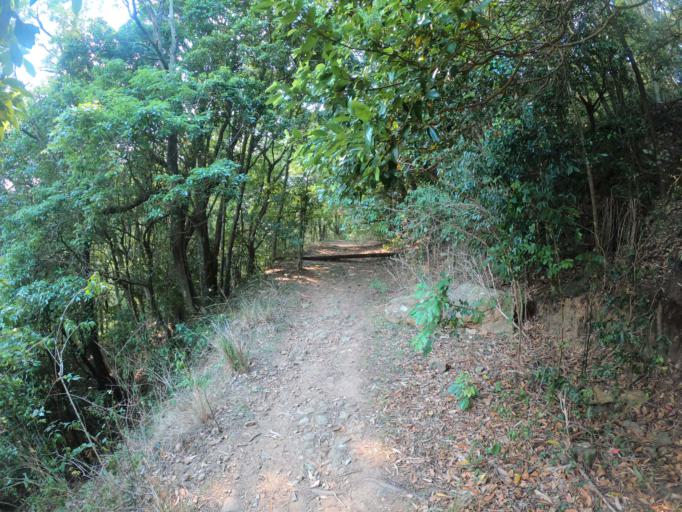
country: AU
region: New South Wales
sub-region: Wollongong
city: Bulli
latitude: -34.3293
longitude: 150.8913
